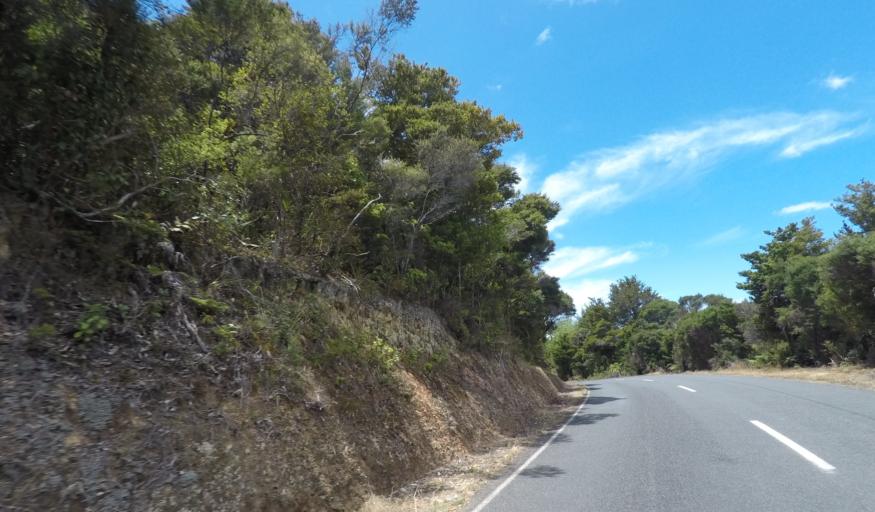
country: NZ
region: Northland
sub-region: Whangarei
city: Ngunguru
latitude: -35.5071
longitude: 174.4386
